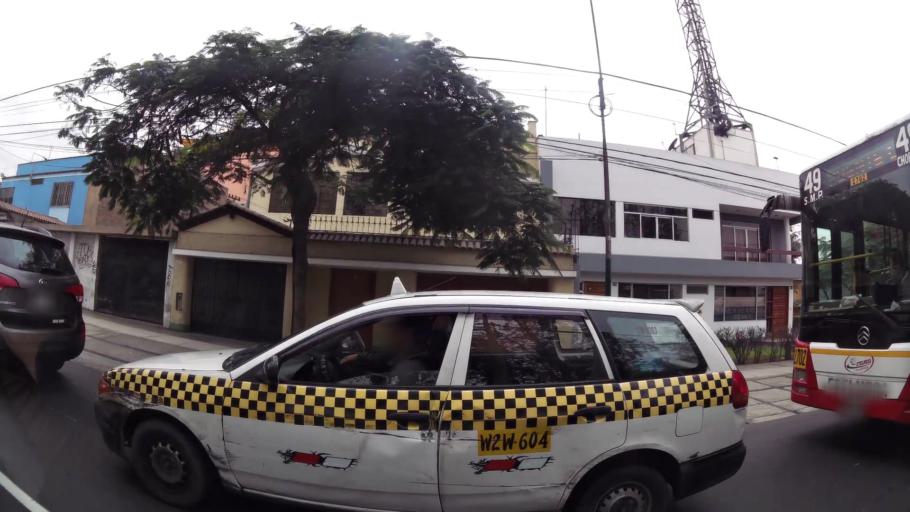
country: PE
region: Lima
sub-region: Lima
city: Surco
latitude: -12.1335
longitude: -76.9832
